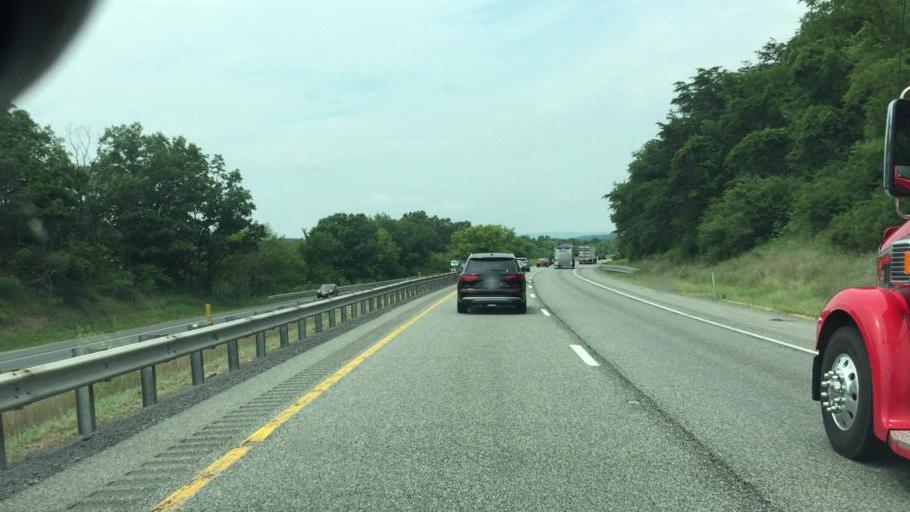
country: US
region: Maryland
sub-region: Washington County
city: Hancock
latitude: 39.6729
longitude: -78.0806
